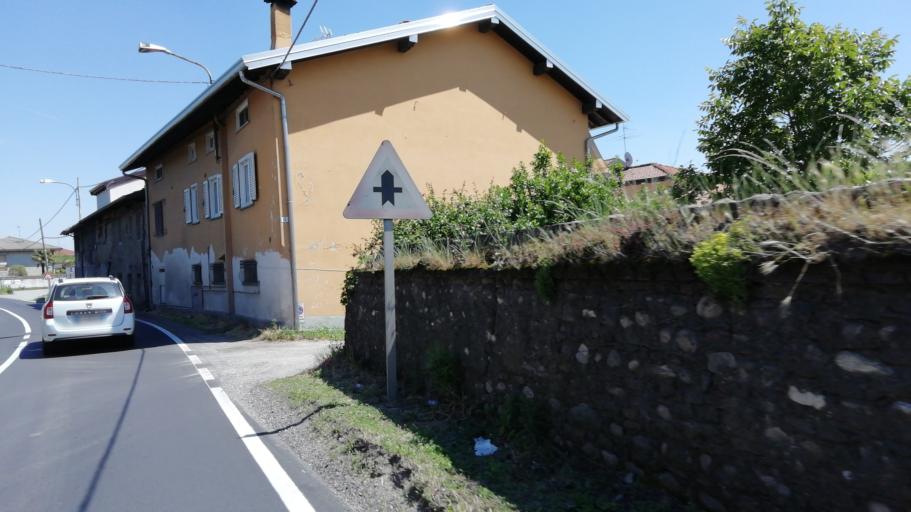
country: IT
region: Piedmont
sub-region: Provincia di Novara
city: Oleggio
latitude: 45.5920
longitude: 8.6535
